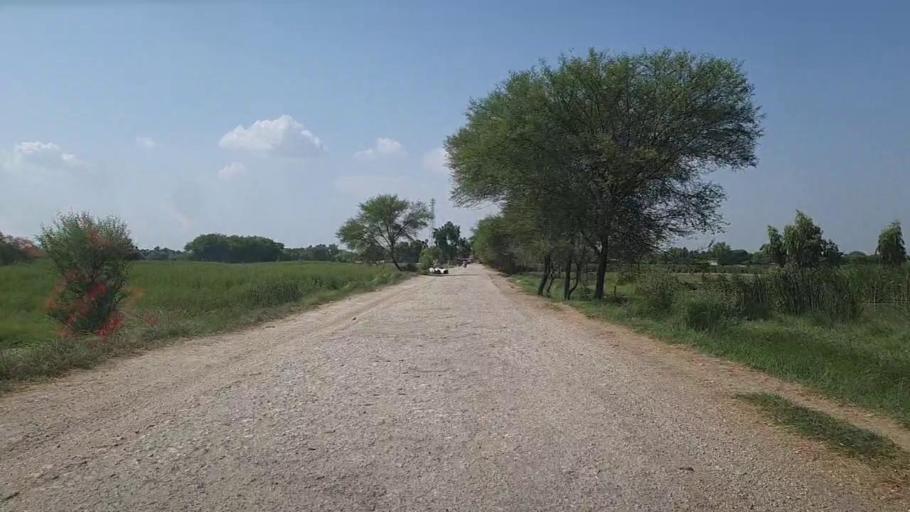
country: PK
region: Sindh
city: Khairpur
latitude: 28.1167
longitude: 69.6174
